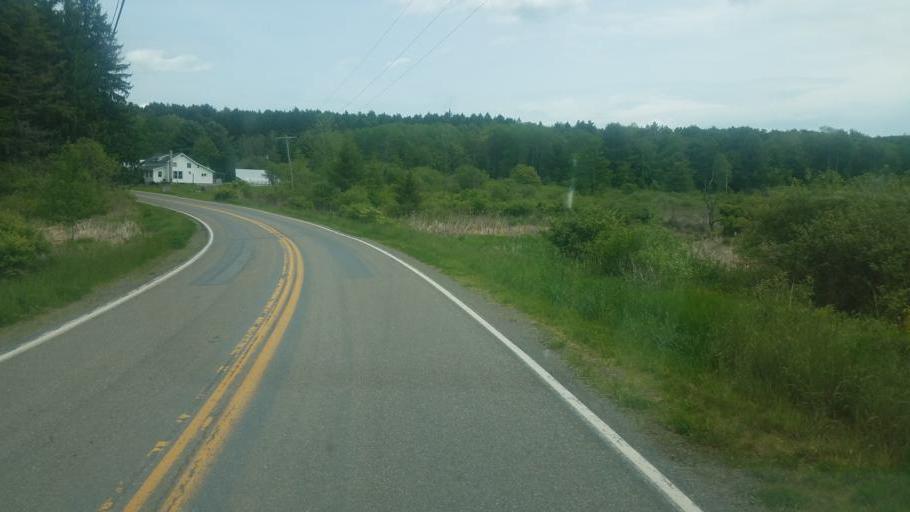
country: US
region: Pennsylvania
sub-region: Tioga County
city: Wellsboro
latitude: 41.6960
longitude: -77.4131
